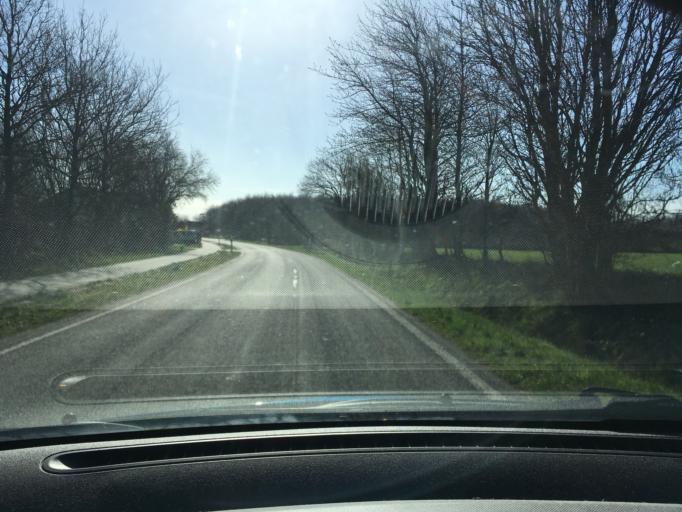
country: DE
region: Schleswig-Holstein
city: Borgwedel
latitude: 54.4962
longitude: 9.6513
